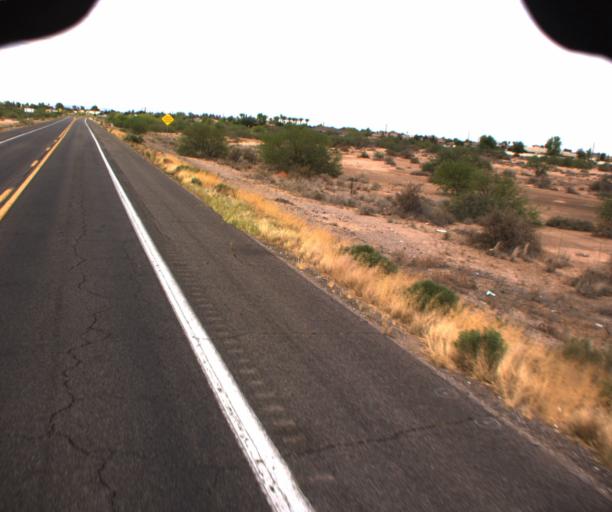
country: US
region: Arizona
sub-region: Maricopa County
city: Sun Lakes
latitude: 33.2011
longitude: -111.8349
